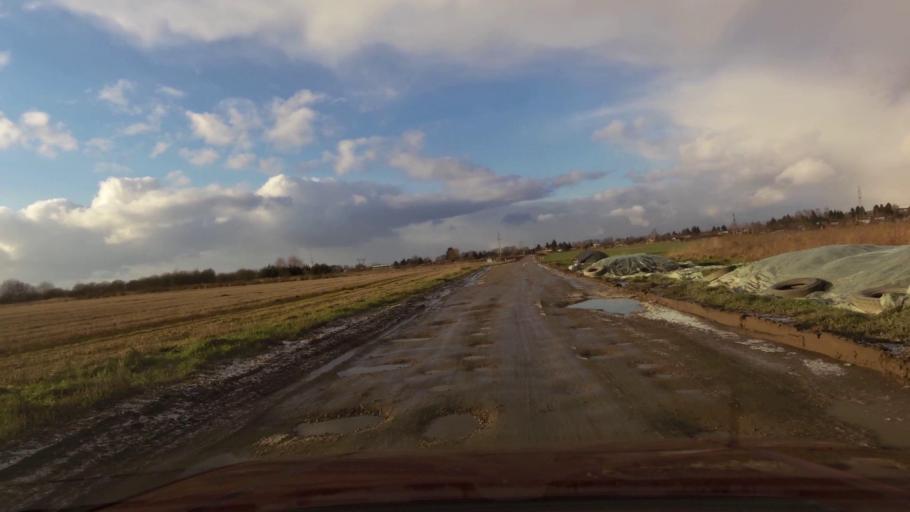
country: PL
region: West Pomeranian Voivodeship
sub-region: Koszalin
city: Koszalin
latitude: 54.1661
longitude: 16.1722
